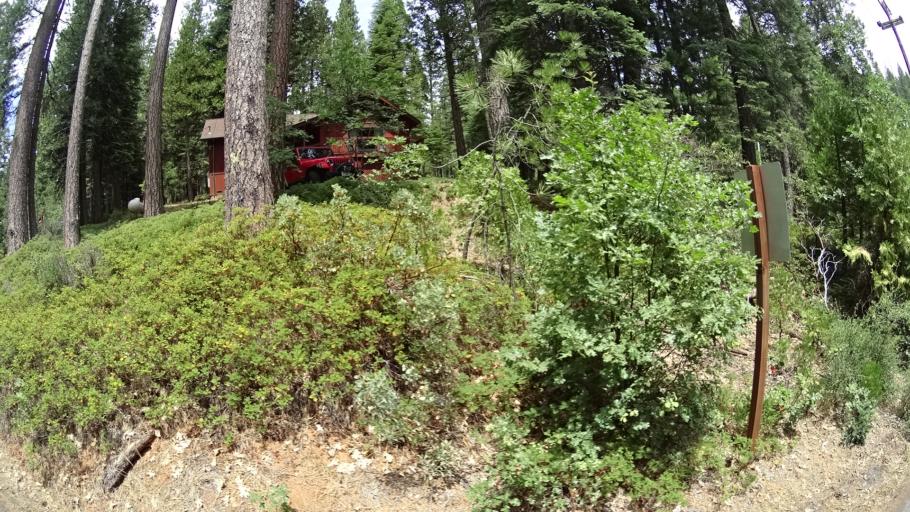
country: US
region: California
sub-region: Calaveras County
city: Arnold
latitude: 38.2386
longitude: -120.3436
